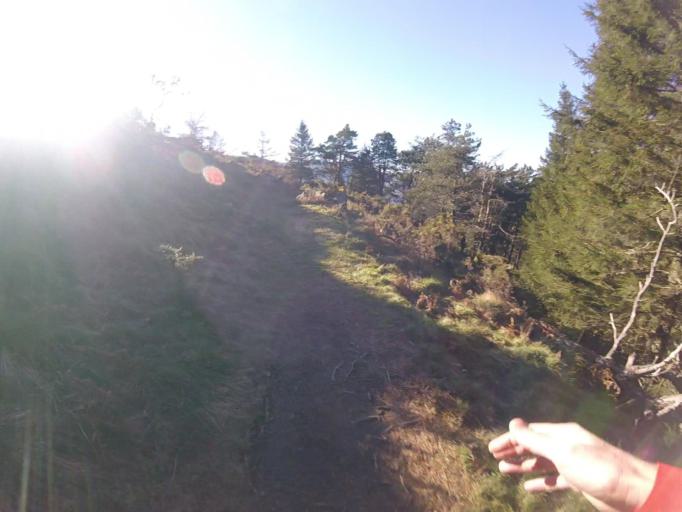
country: ES
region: Basque Country
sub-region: Provincia de Guipuzcoa
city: Irun
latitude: 43.2764
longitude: -1.7972
